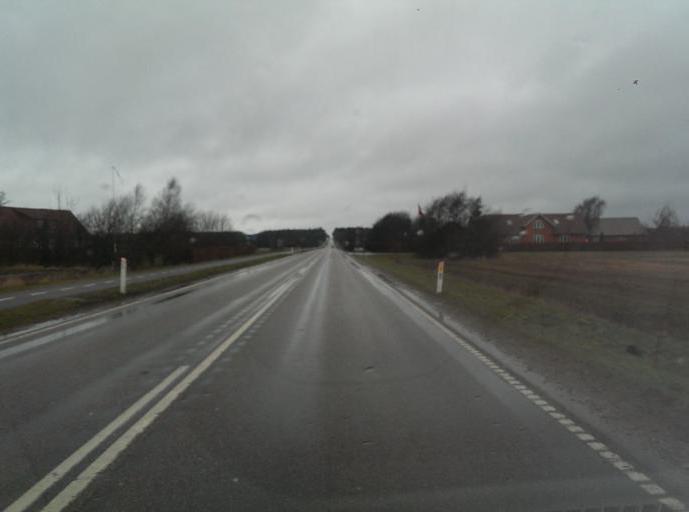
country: DK
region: Central Jutland
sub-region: Ringkobing-Skjern Kommune
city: Skjern
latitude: 55.9766
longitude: 8.4651
